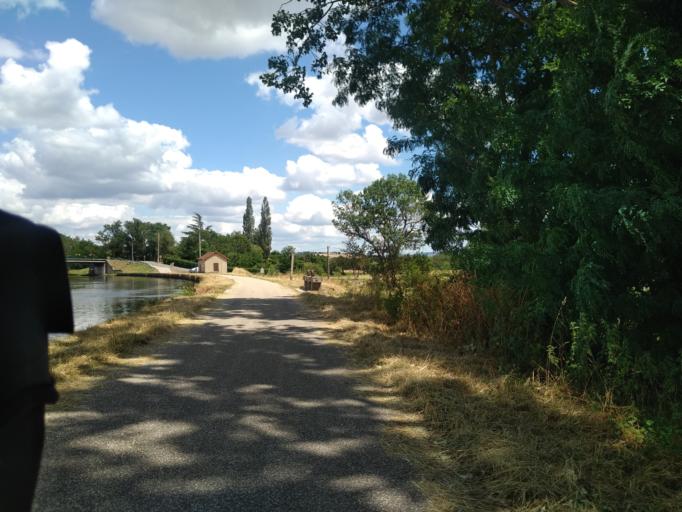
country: FR
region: Rhone-Alpes
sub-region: Departement de la Loire
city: Briennon
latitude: 46.1471
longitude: 4.0869
